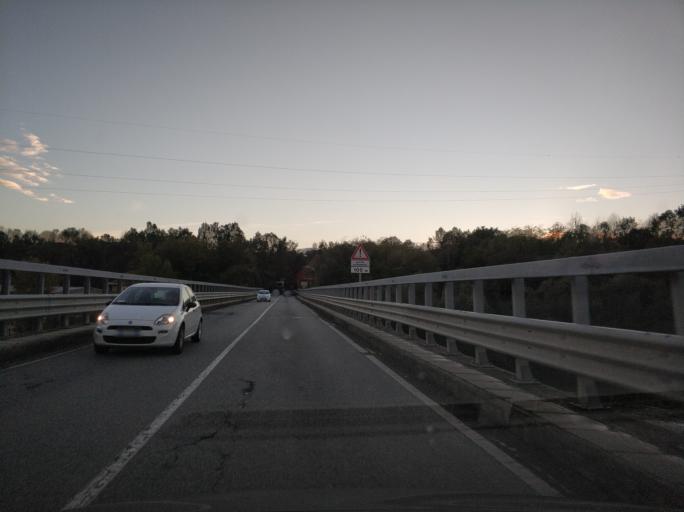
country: IT
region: Piedmont
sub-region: Provincia di Torino
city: Robassomero
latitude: 45.2045
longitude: 7.5727
